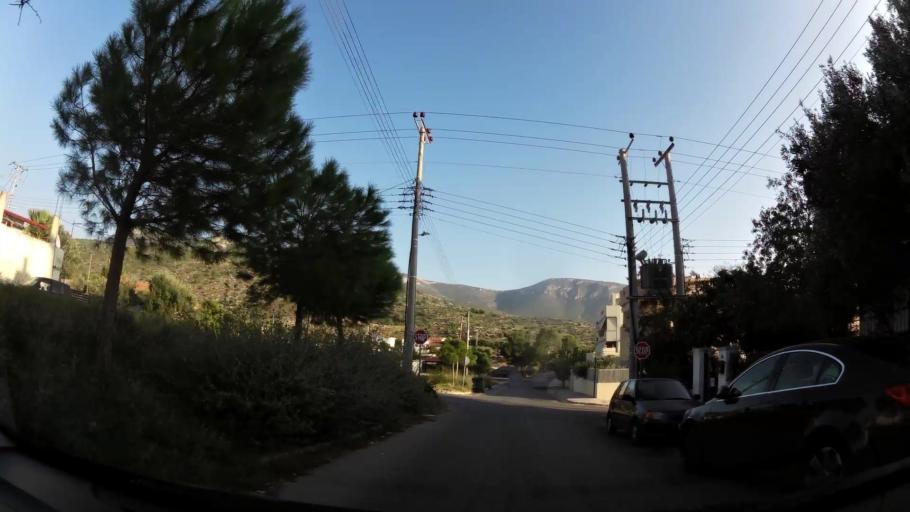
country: GR
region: Attica
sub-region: Nomarchia Athinas
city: Argyroupoli
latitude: 37.9026
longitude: 23.7736
